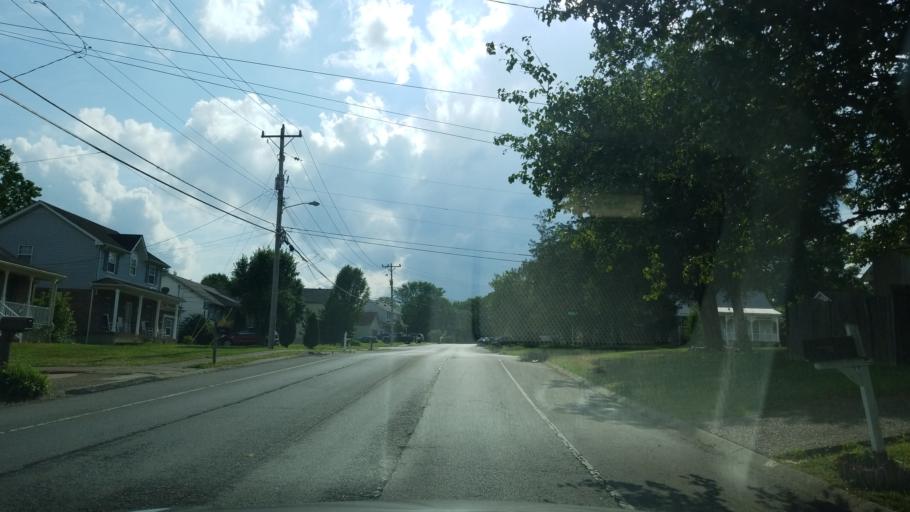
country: US
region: Tennessee
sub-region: Rutherford County
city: La Vergne
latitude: 36.0738
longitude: -86.5973
